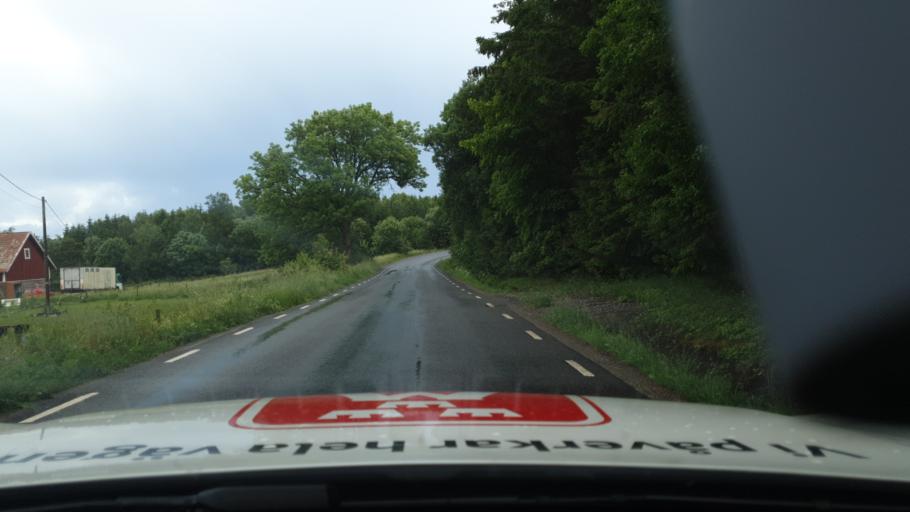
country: SE
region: Vaestra Goetaland
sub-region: Falkopings Kommun
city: Falkoeping
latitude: 58.0585
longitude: 13.6123
